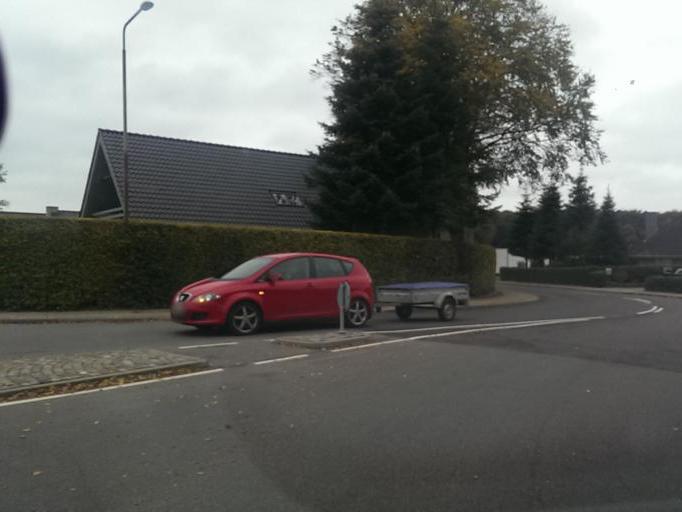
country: DK
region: South Denmark
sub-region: Esbjerg Kommune
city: Bramming
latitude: 55.4684
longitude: 8.7088
